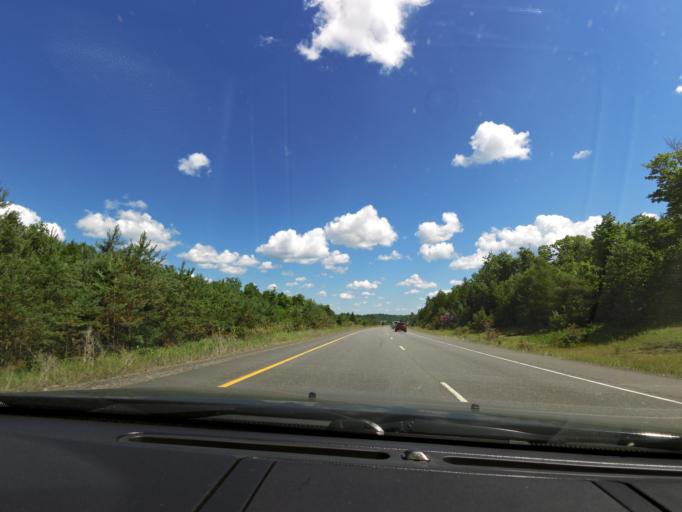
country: CA
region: Ontario
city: Huntsville
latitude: 45.2245
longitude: -79.3112
